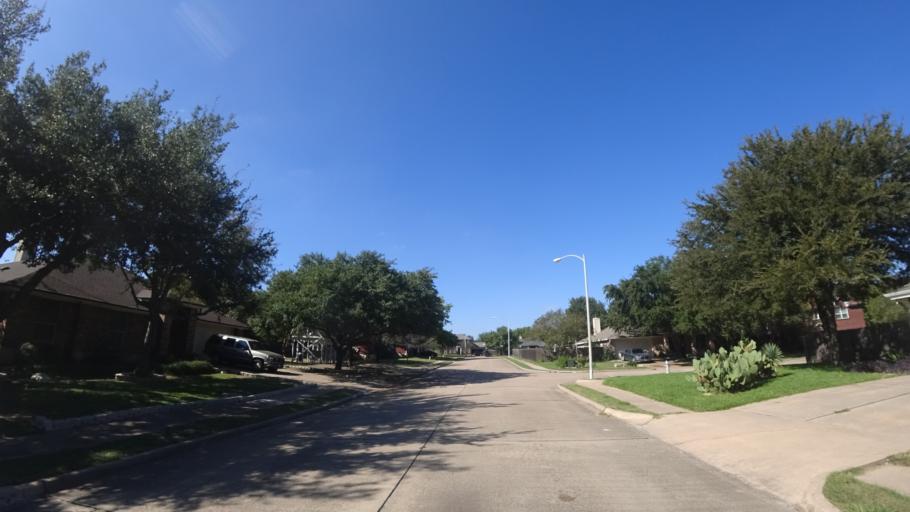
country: US
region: Texas
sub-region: Travis County
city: Manor
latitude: 30.3507
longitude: -97.6143
